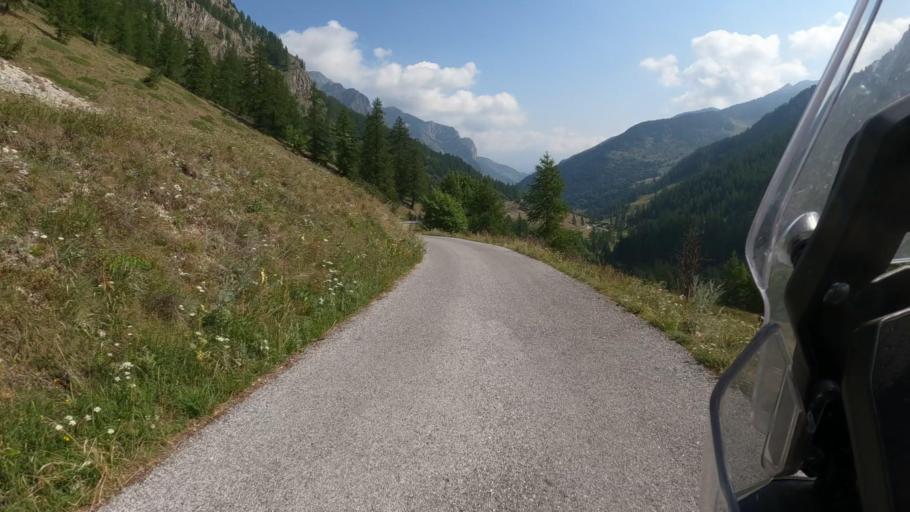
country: IT
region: Piedmont
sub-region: Provincia di Cuneo
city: Canosio
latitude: 44.4159
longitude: 7.0426
